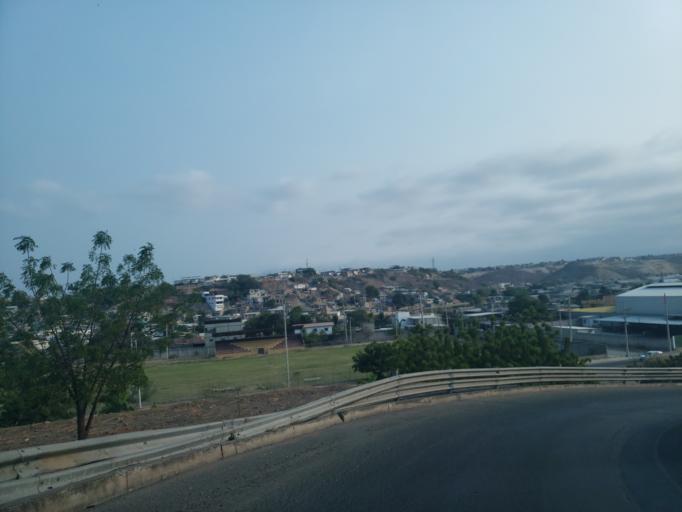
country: EC
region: Manabi
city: Manta
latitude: -0.9550
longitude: -80.7272
